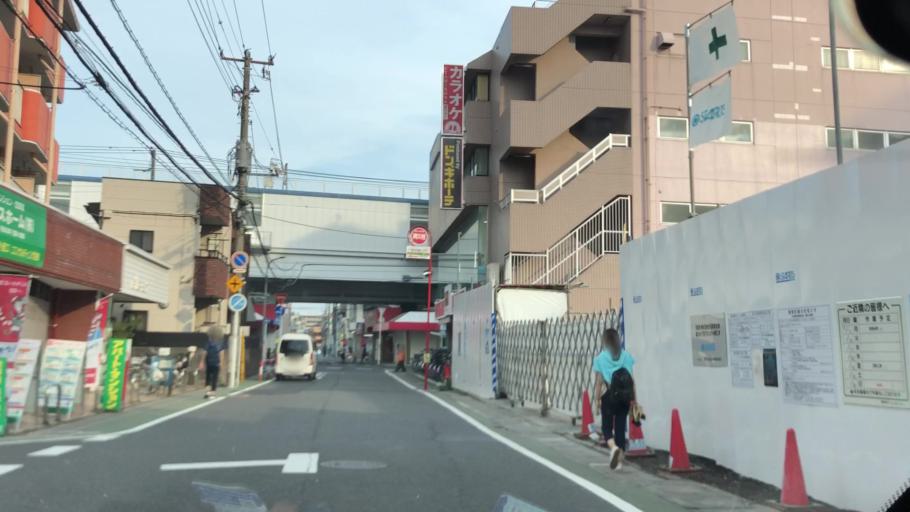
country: JP
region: Tokyo
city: Urayasu
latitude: 35.6735
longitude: 139.9020
